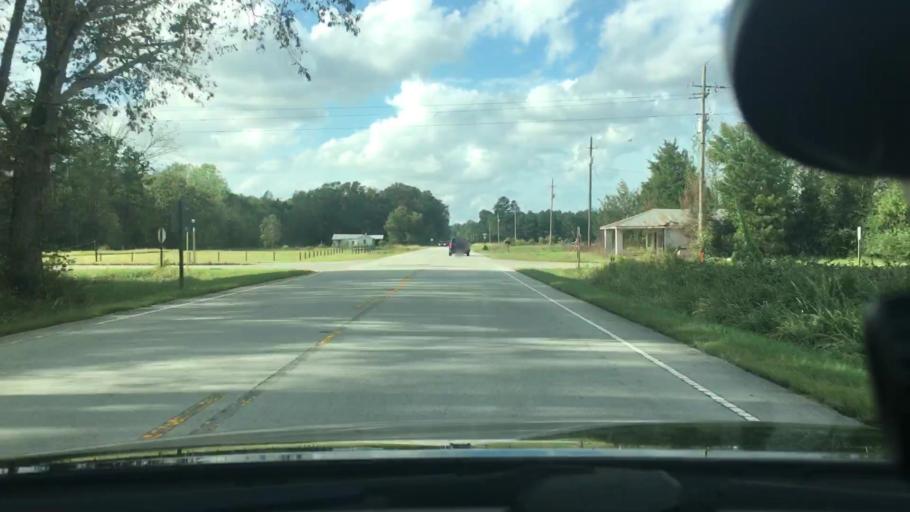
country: US
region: North Carolina
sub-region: Craven County
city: Vanceboro
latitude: 35.4004
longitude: -77.2378
